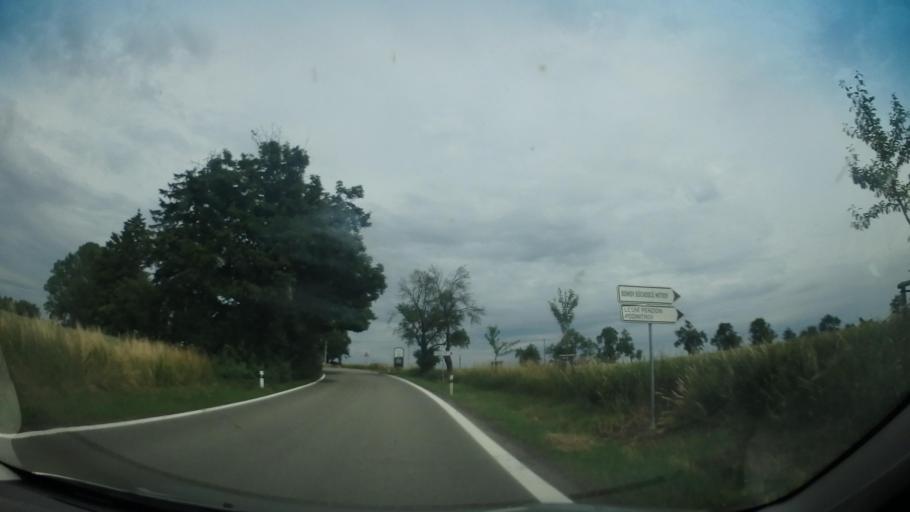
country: CZ
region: Vysocina
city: Bystrice nad Pernstejnem
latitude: 49.4611
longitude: 16.2248
